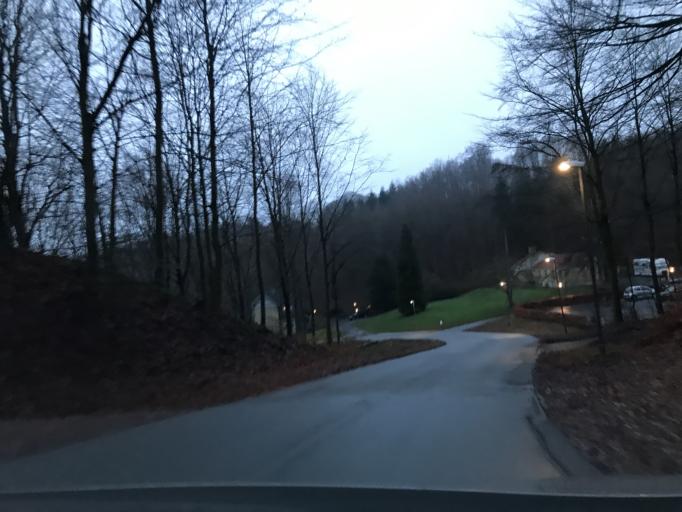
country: DK
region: South Denmark
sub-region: Vejle Kommune
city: Brejning
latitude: 55.6849
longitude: 9.7644
